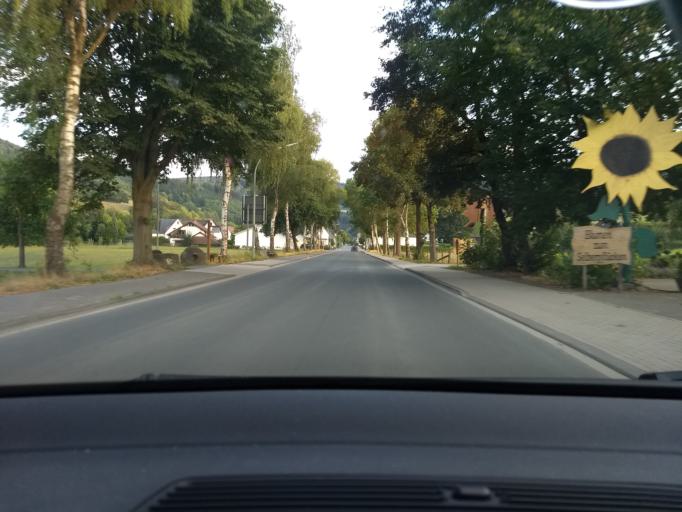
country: DE
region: North Rhine-Westphalia
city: Eslohe
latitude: 51.3320
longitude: 8.1593
